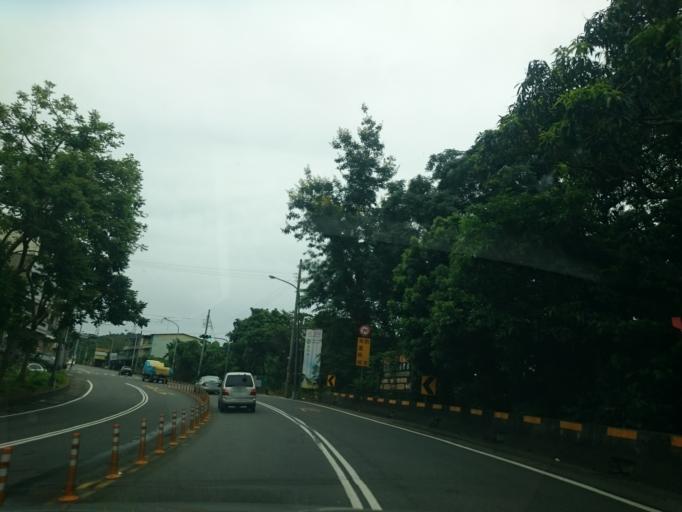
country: TW
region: Taiwan
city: Lugu
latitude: 23.8307
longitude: 120.7158
